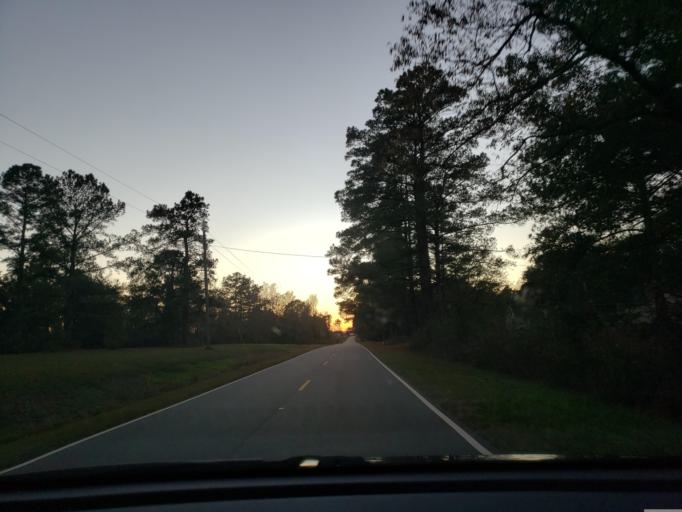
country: US
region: North Carolina
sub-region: Duplin County
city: Beulaville
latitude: 34.7544
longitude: -77.6958
